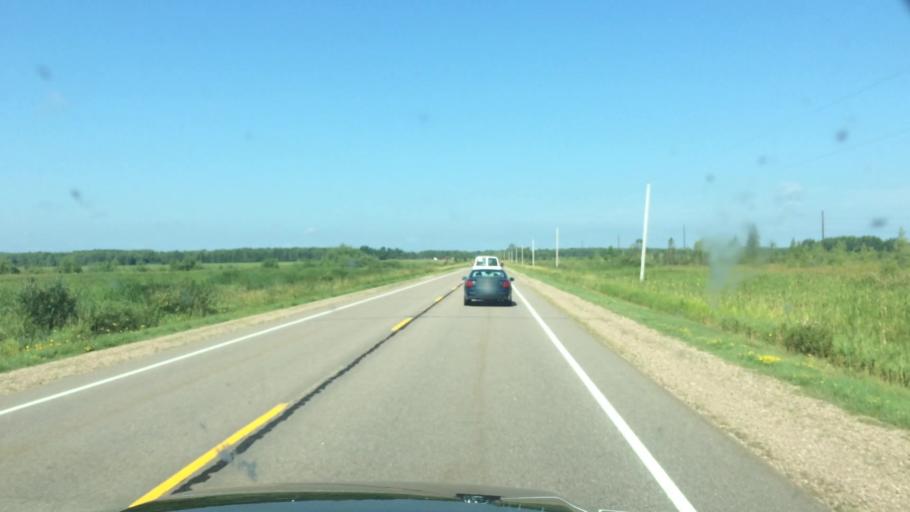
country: US
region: Wisconsin
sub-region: Langlade County
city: Antigo
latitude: 45.1470
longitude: -89.3979
